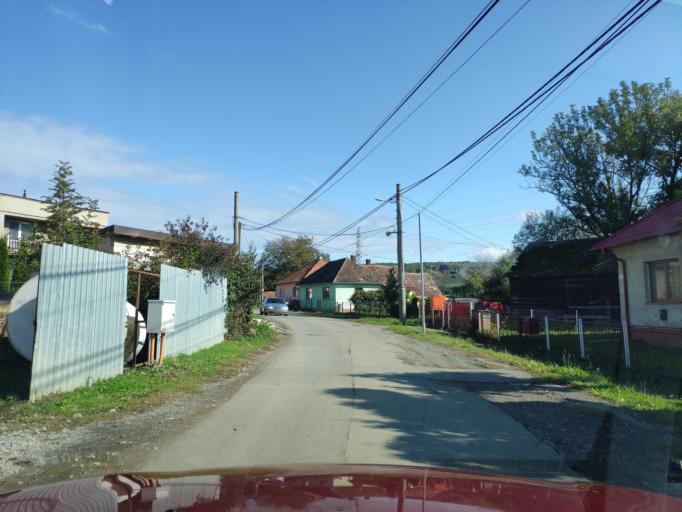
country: SK
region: Presovsky
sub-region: Okres Presov
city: Presov
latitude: 48.9240
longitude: 21.2623
